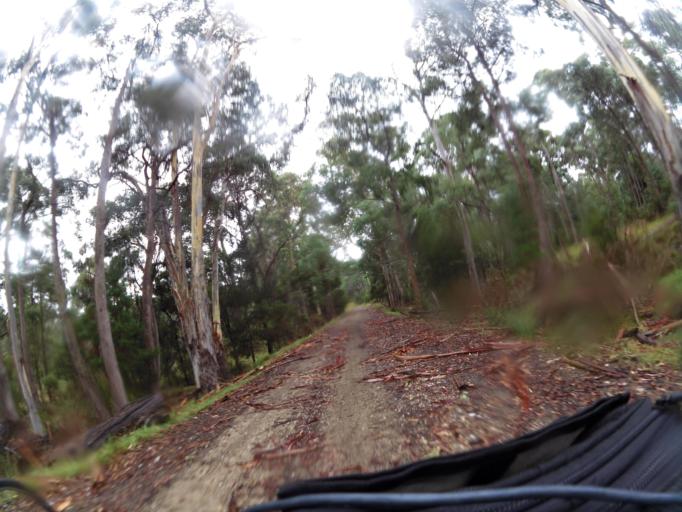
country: AU
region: New South Wales
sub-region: Greater Hume Shire
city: Holbrook
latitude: -36.1707
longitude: 147.4958
